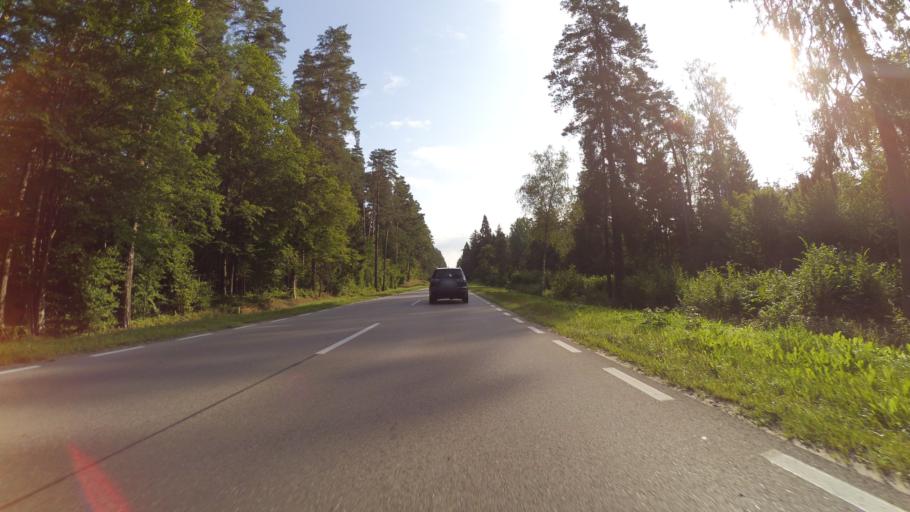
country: PL
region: Podlasie
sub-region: Powiat bialostocki
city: Czarna Bialostocka
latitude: 53.3204
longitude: 23.3392
